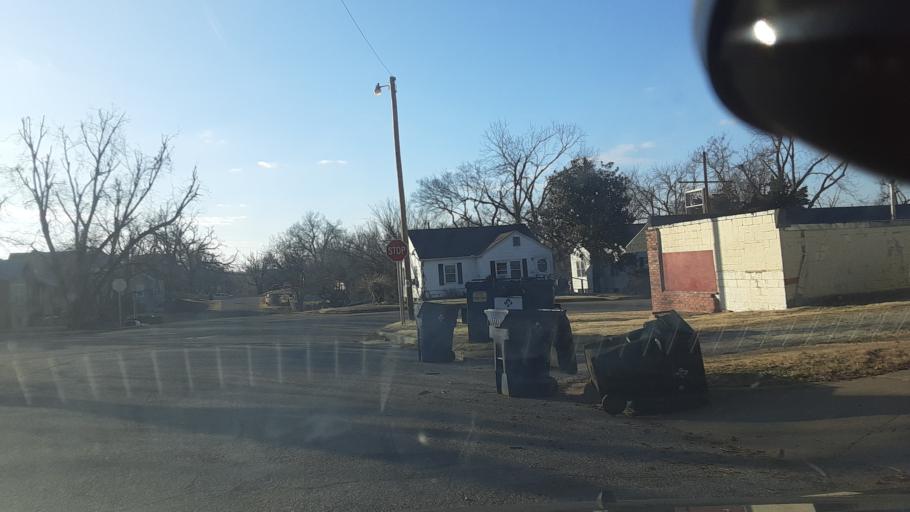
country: US
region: Oklahoma
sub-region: Logan County
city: Guthrie
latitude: 35.8822
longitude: -97.4237
